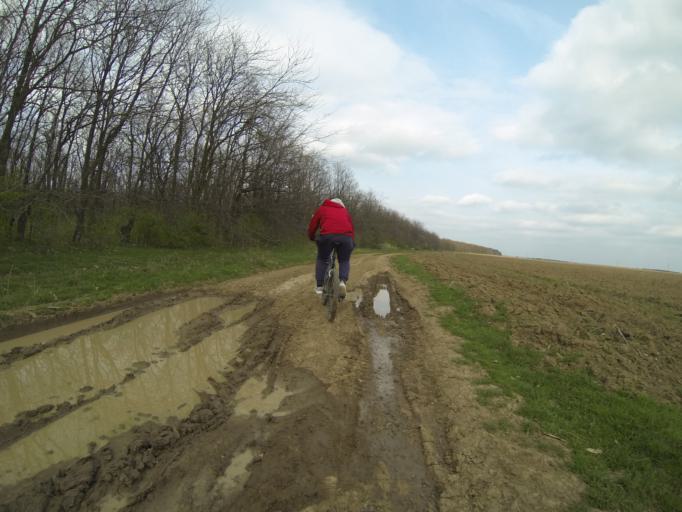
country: RO
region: Dolj
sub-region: Comuna Podari
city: Podari
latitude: 44.2466
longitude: 23.7371
